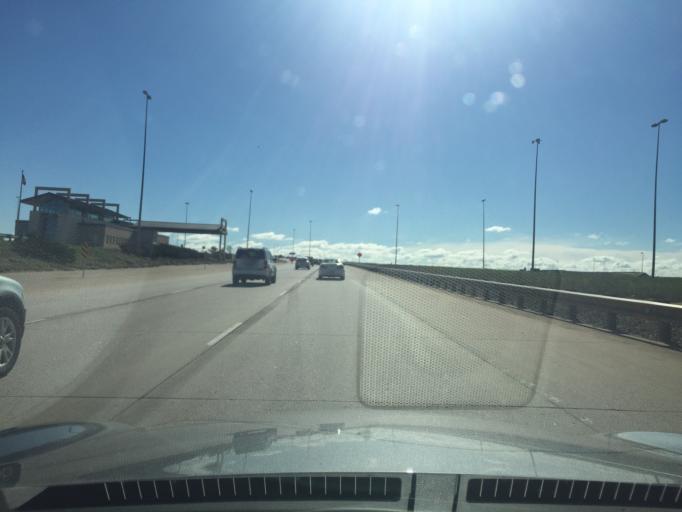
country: US
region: Colorado
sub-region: Adams County
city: Aurora
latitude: 39.8332
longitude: -104.7246
